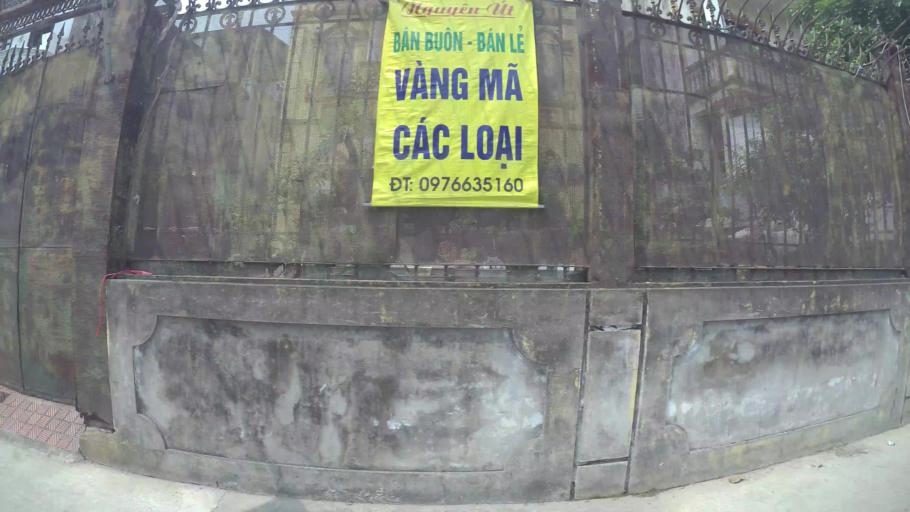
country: VN
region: Ha Noi
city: Tay Ho
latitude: 21.0871
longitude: 105.8033
